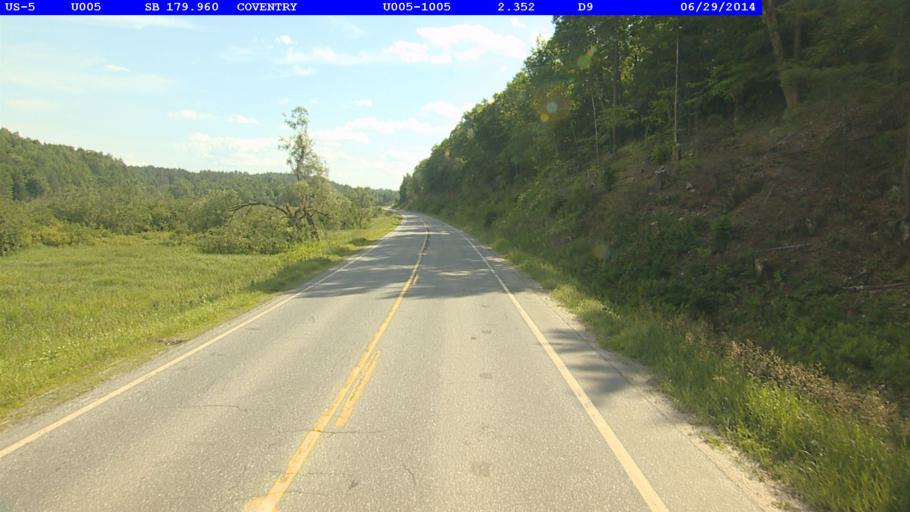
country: US
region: Vermont
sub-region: Orleans County
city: Newport
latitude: 44.8890
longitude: -72.2469
